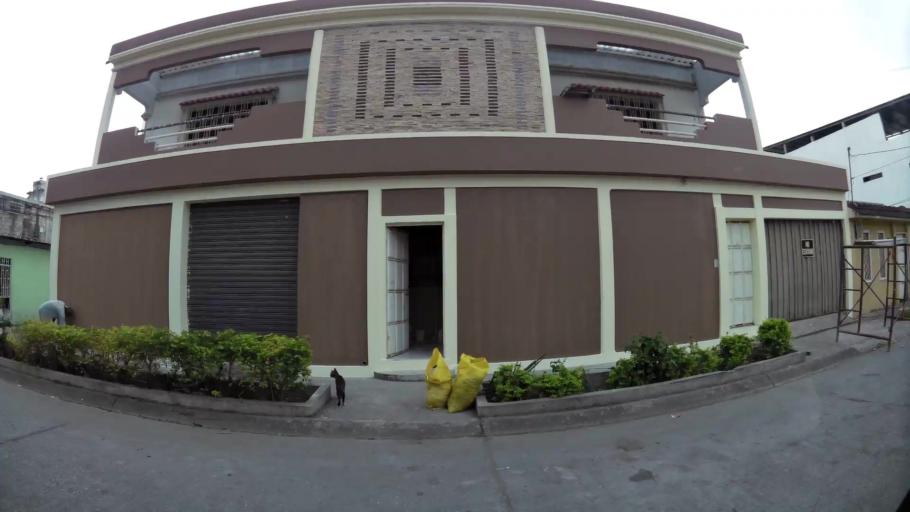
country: EC
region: Guayas
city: Eloy Alfaro
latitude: -2.1227
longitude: -79.8851
